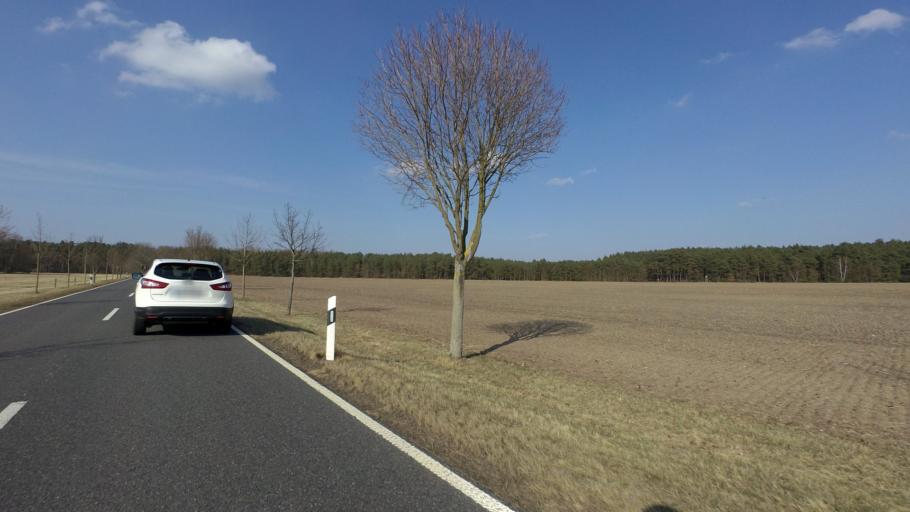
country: DE
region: Brandenburg
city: Trebbin
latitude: 52.2263
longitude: 13.1381
